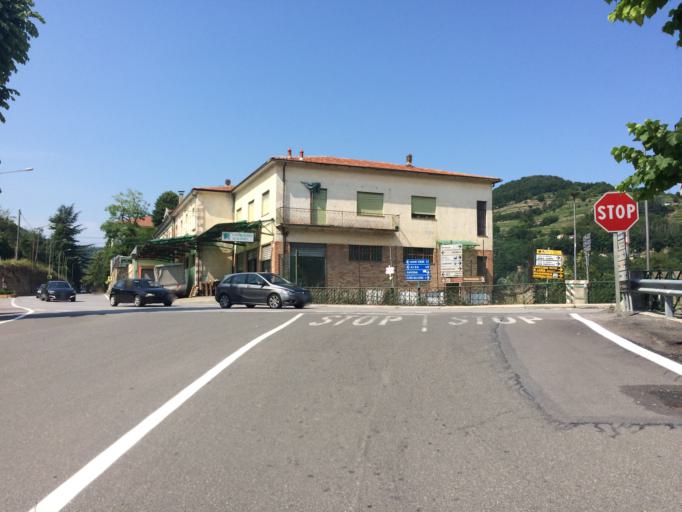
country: IT
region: Piedmont
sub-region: Provincia di Cuneo
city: Cortemilia
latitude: 44.5805
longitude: 8.1923
